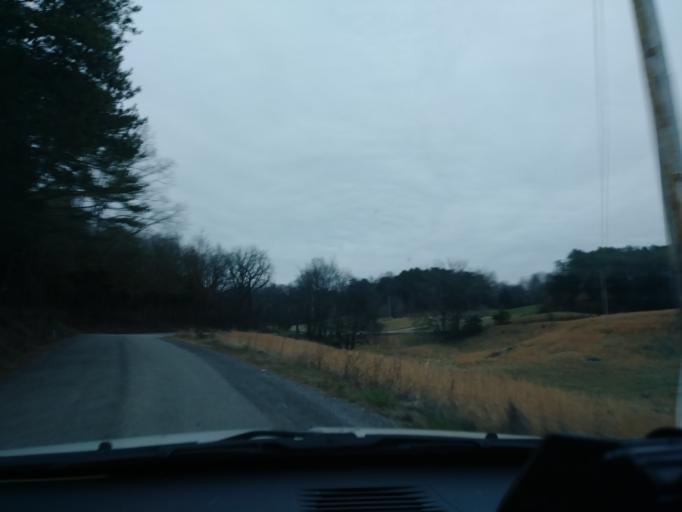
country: US
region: Tennessee
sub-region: Greene County
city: Greeneville
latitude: 36.0819
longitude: -82.8912
